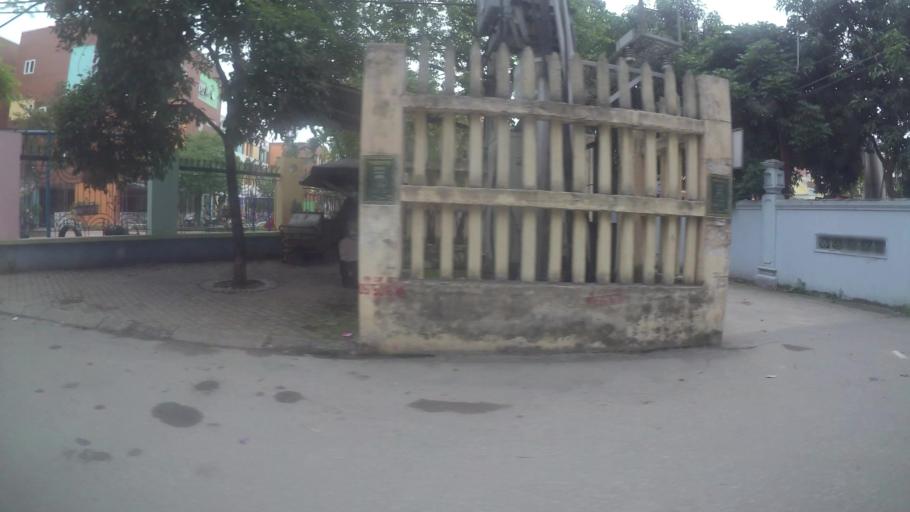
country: VN
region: Ha Noi
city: Tay Ho
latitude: 21.0673
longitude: 105.8228
